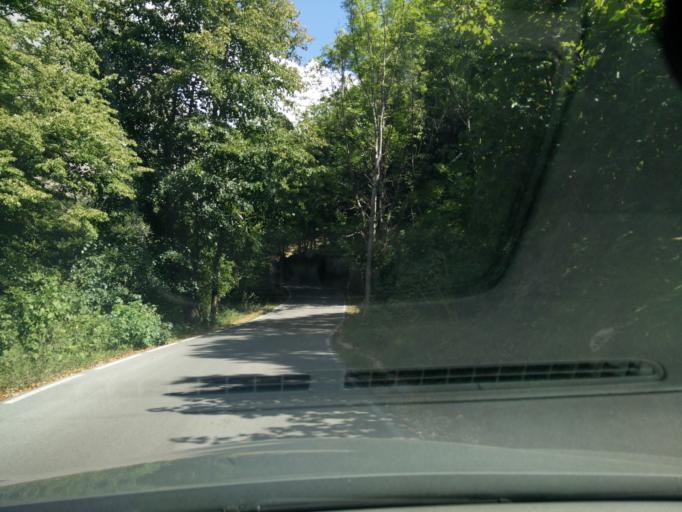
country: ES
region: Castille and Leon
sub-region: Provincia de Leon
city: Posada de Valdeon
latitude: 43.1914
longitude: -4.9091
